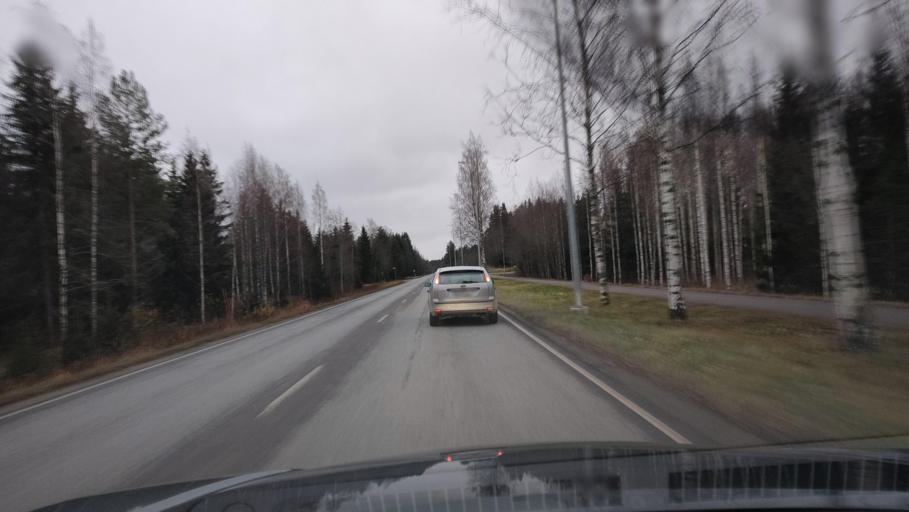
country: FI
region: Southern Ostrobothnia
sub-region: Suupohja
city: Kauhajoki
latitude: 62.4115
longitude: 22.1688
